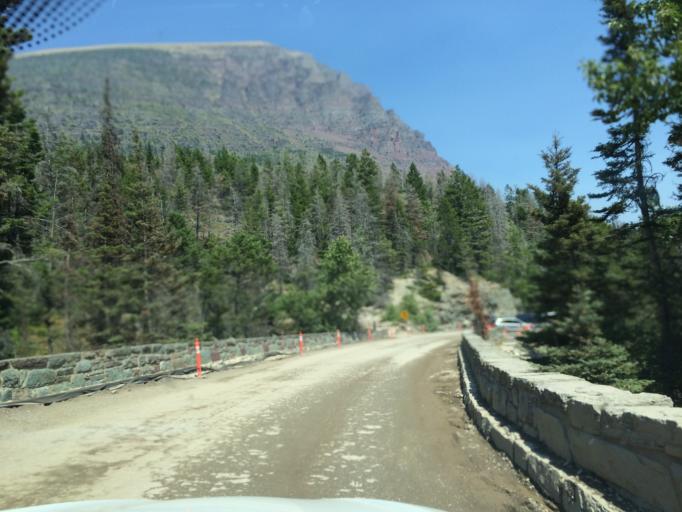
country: US
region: Montana
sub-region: Glacier County
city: Browning
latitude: 48.6781
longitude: -113.5961
